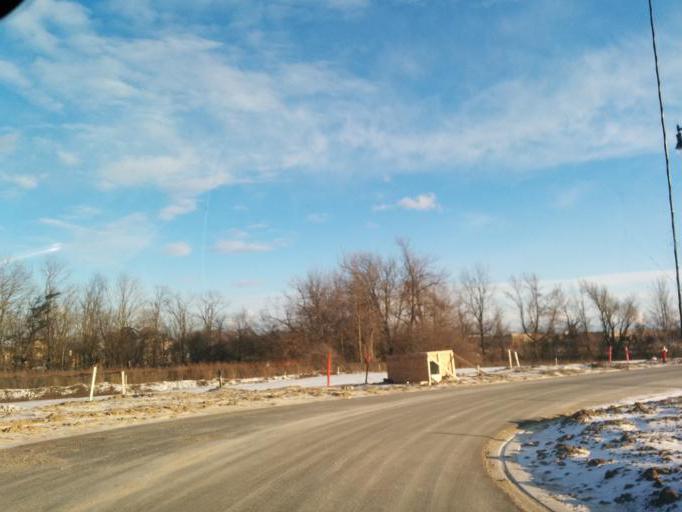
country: CA
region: Ontario
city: Brampton
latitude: 43.6626
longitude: -79.8169
